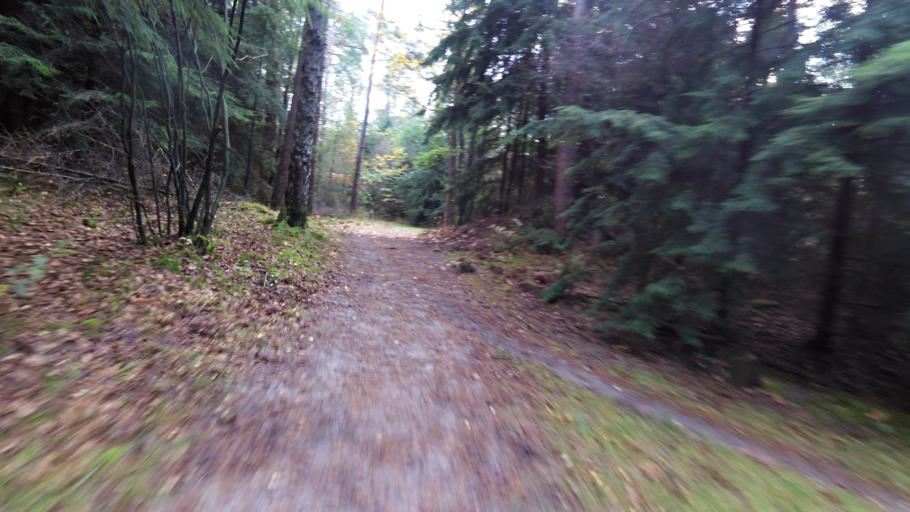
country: NL
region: Gelderland
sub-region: Gemeente Nunspeet
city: Nunspeet
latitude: 52.3688
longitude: 5.8206
